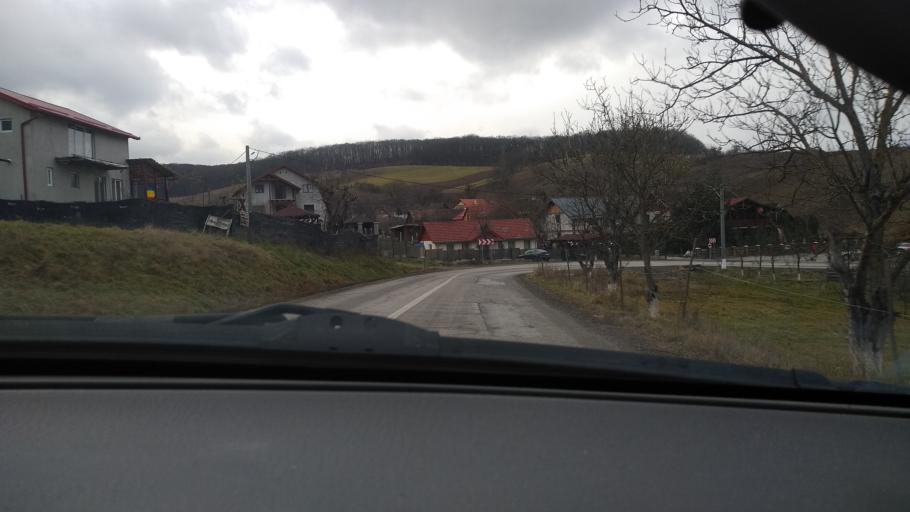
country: RO
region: Mures
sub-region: Comuna Pasareni
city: Pasareni
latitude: 46.5389
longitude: 24.6942
